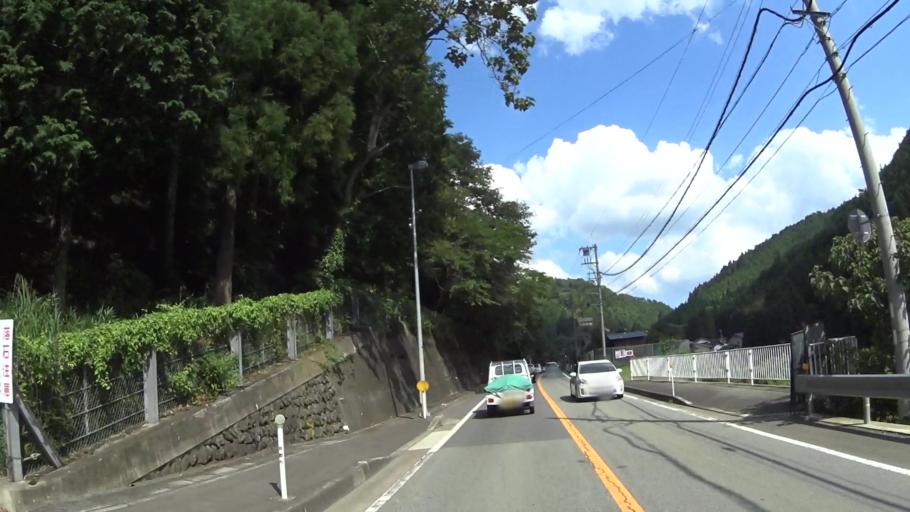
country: JP
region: Kyoto
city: Kameoka
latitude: 35.1215
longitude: 135.6492
